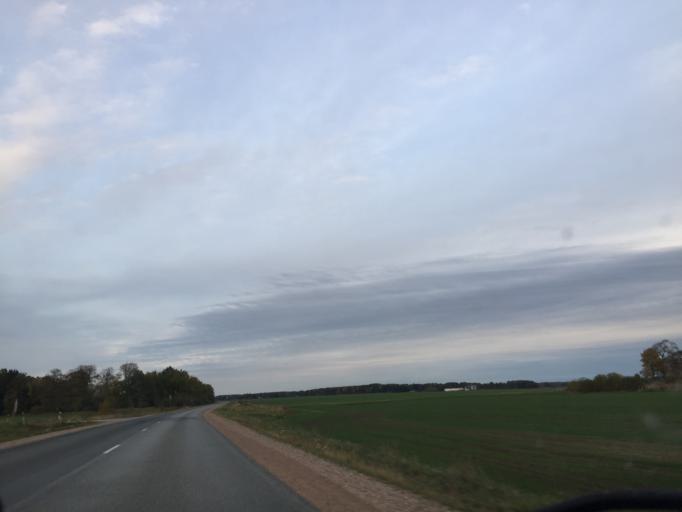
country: LV
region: Dobeles Rajons
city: Dobele
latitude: 56.7015
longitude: 23.3757
